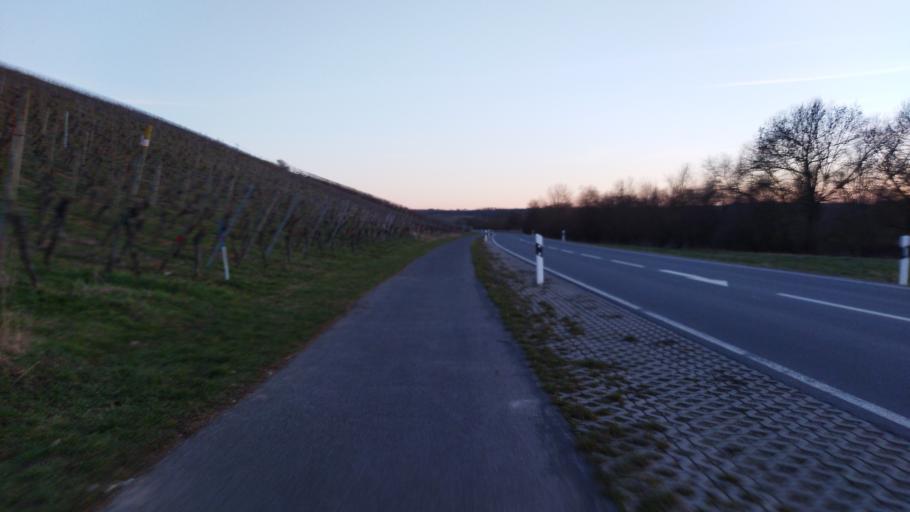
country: DE
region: Bavaria
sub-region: Regierungsbezirk Unterfranken
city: Wipfeld
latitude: 49.9007
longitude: 10.1907
